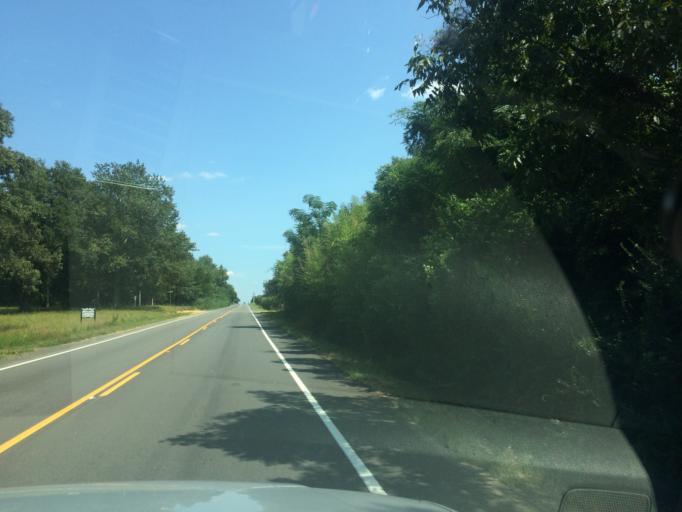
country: US
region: South Carolina
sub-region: Aiken County
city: Aiken
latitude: 33.5725
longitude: -81.5534
